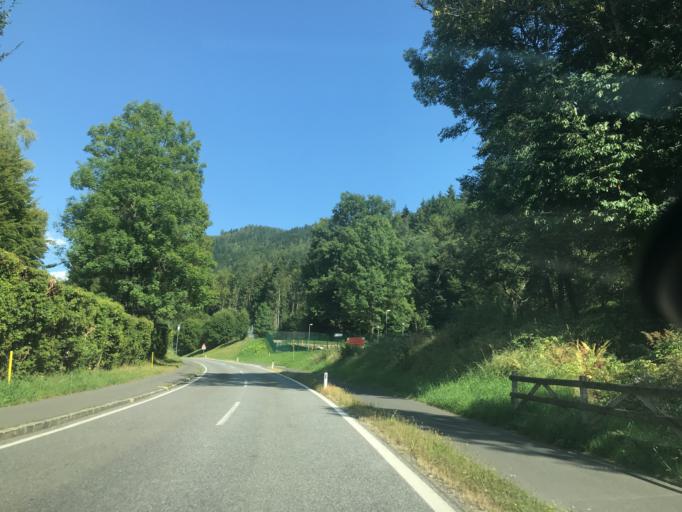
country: AT
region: Carinthia
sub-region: Politischer Bezirk Villach Land
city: Wernberg
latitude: 46.6525
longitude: 13.9303
